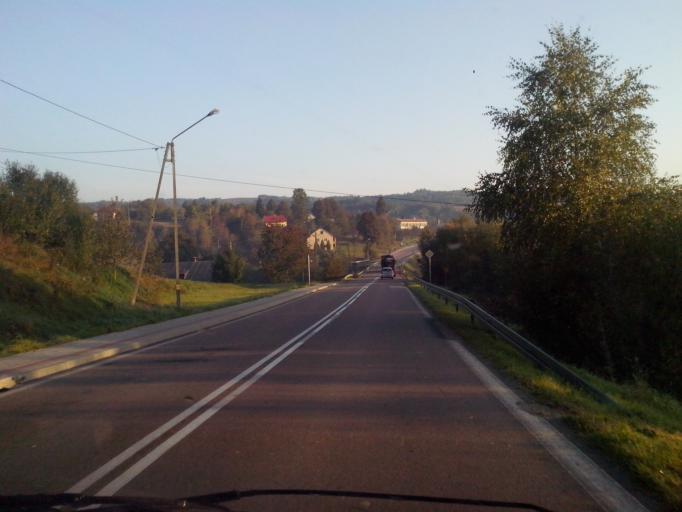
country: PL
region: Subcarpathian Voivodeship
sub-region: Powiat brzozowski
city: Golcowa
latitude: 49.8106
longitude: 22.0403
